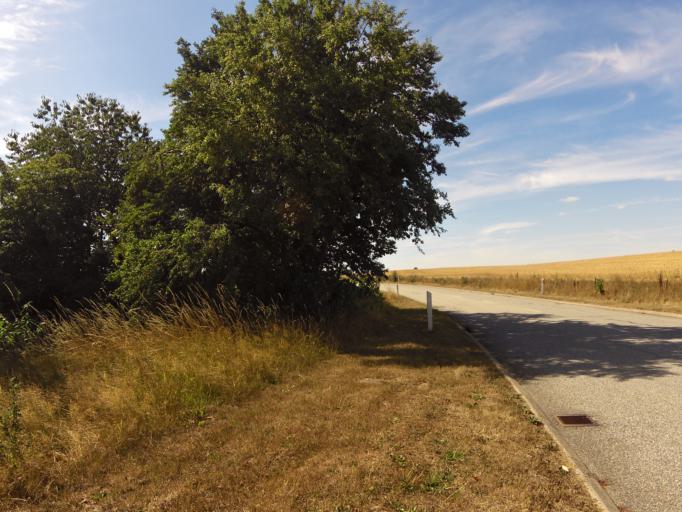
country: DK
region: Capital Region
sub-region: Fredensborg Kommune
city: Niva
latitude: 55.9470
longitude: 12.4979
